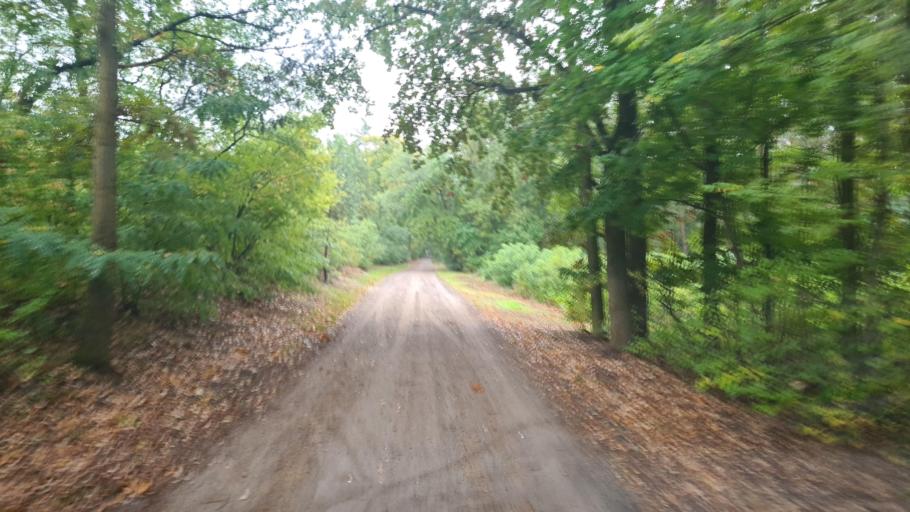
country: DE
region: Brandenburg
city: Storkow
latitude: 52.2260
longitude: 13.9345
